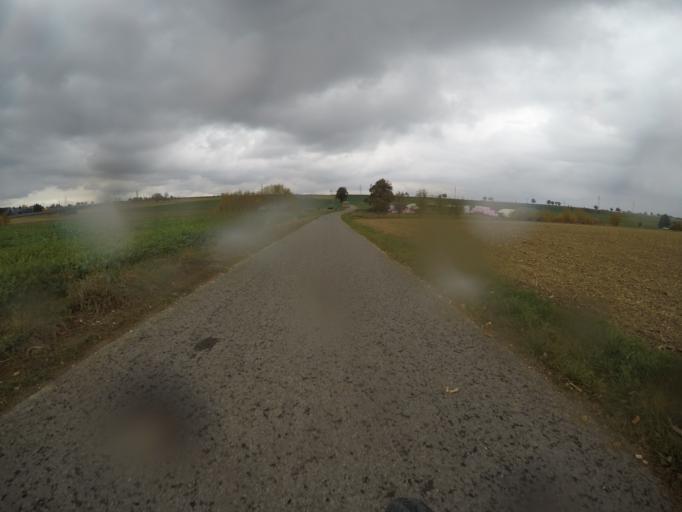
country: DE
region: Baden-Wuerttemberg
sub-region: Regierungsbezirk Stuttgart
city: Herrenberg
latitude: 48.6110
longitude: 8.8574
